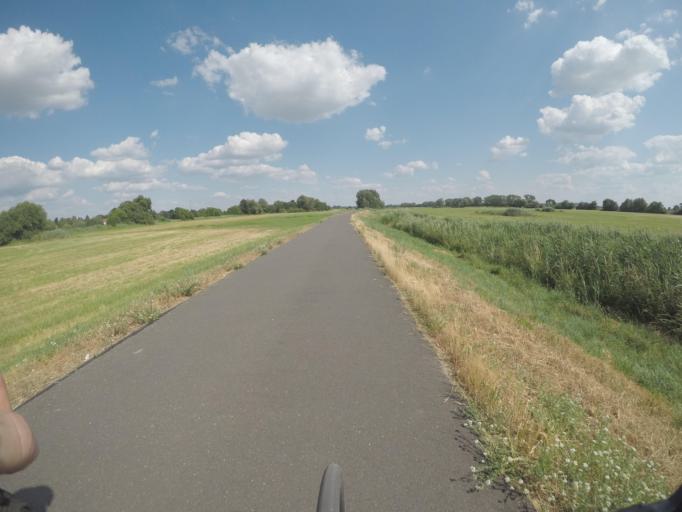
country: DE
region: Brandenburg
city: Ketzin
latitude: 52.4639
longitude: 12.8467
